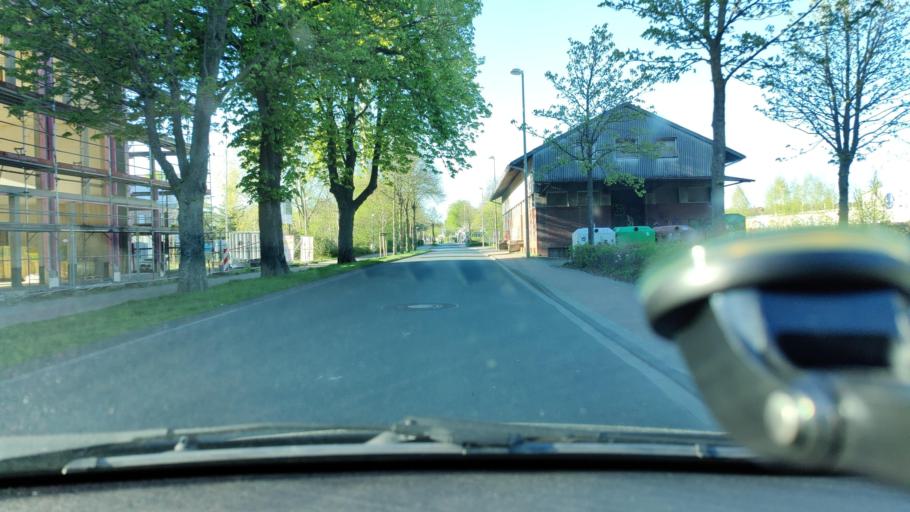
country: DE
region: North Rhine-Westphalia
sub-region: Regierungsbezirk Munster
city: Ahaus
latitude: 52.0798
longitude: 7.0159
